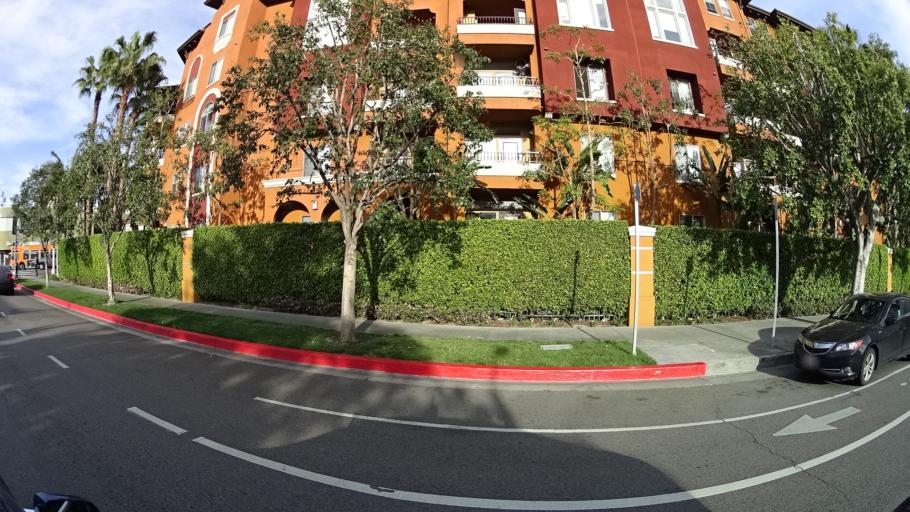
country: US
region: California
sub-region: Los Angeles County
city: West Hollywood
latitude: 34.0694
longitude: -118.3511
